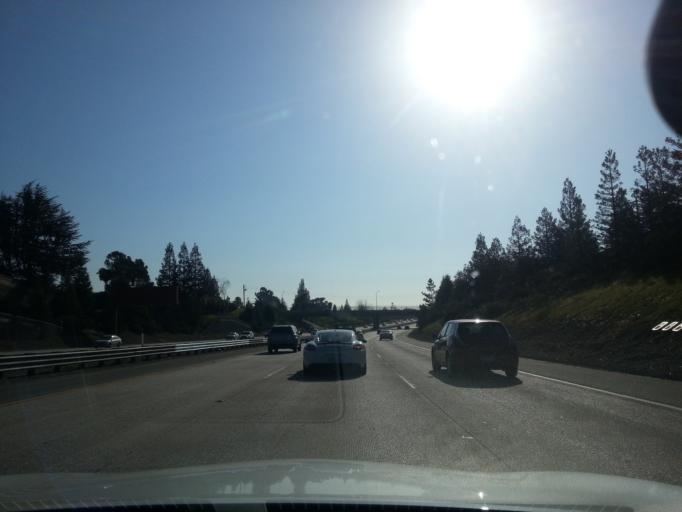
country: US
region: California
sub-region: Santa Clara County
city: Saratoga
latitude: 37.2722
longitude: -121.9968
